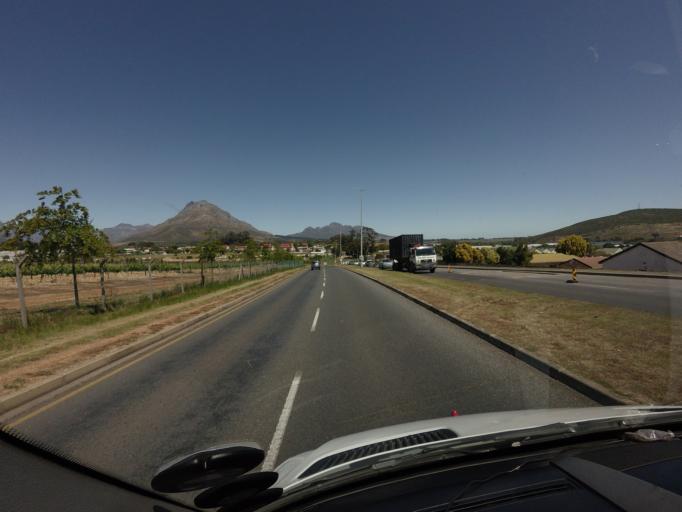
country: ZA
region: Western Cape
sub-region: Cape Winelands District Municipality
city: Stellenbosch
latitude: -33.9204
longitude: 18.8585
